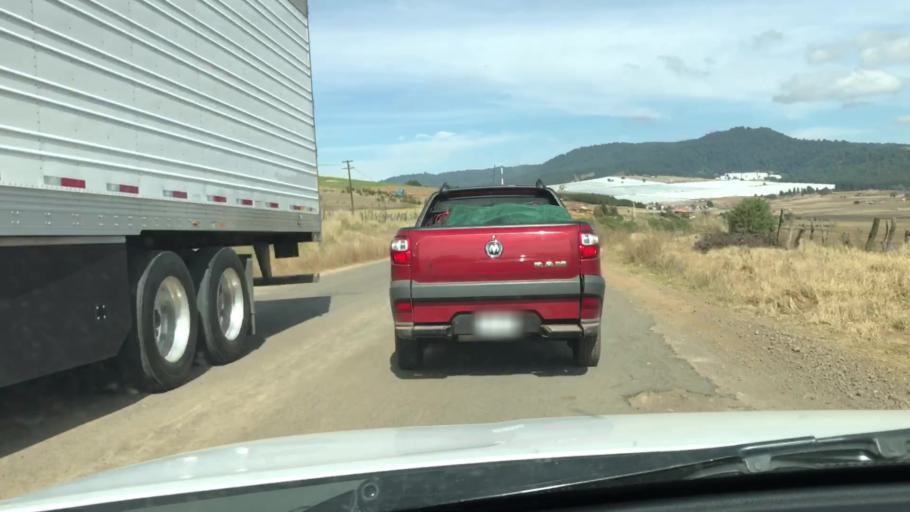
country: MX
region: Jalisco
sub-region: Amacueca
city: Tepec
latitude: 20.0142
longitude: -103.6950
